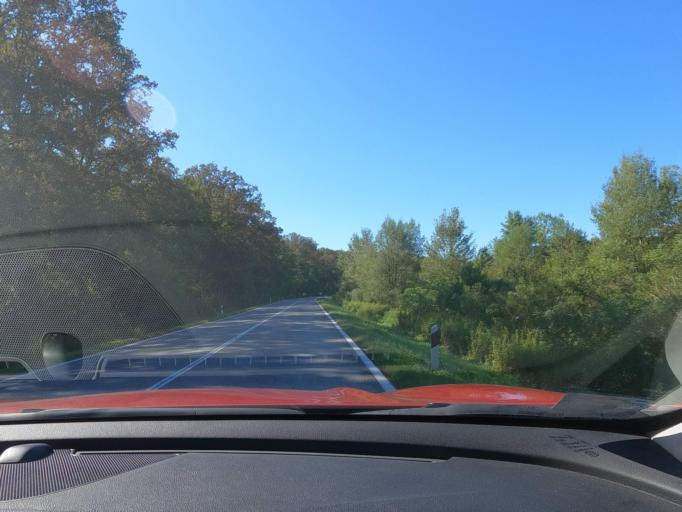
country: HR
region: Sisacko-Moslavacka
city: Osekovo
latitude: 45.5096
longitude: 16.5275
